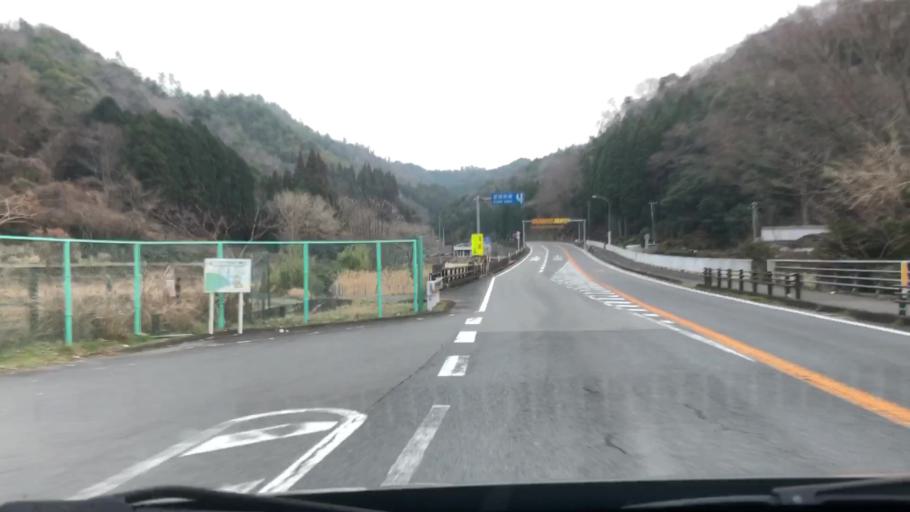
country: JP
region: Oita
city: Tsukumiura
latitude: 32.9961
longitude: 131.7618
